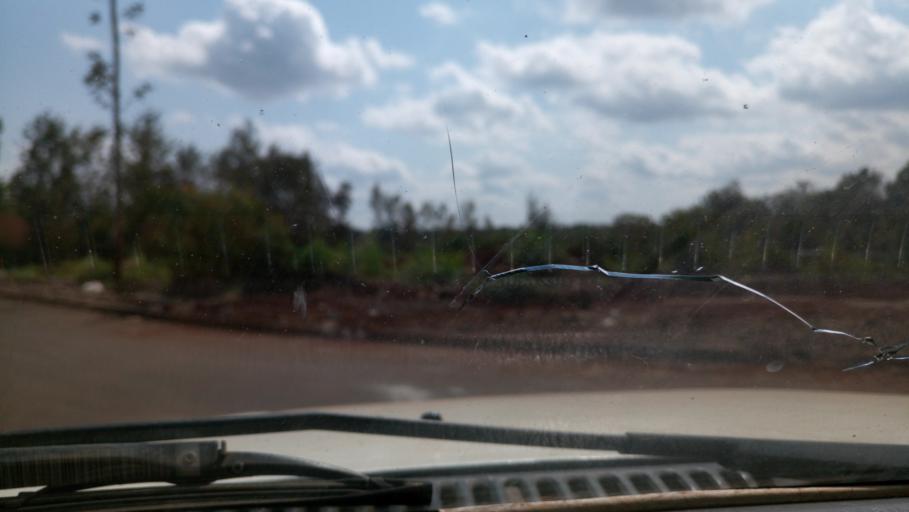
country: KE
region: Nairobi Area
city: Thika
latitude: -0.9358
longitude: 37.1373
